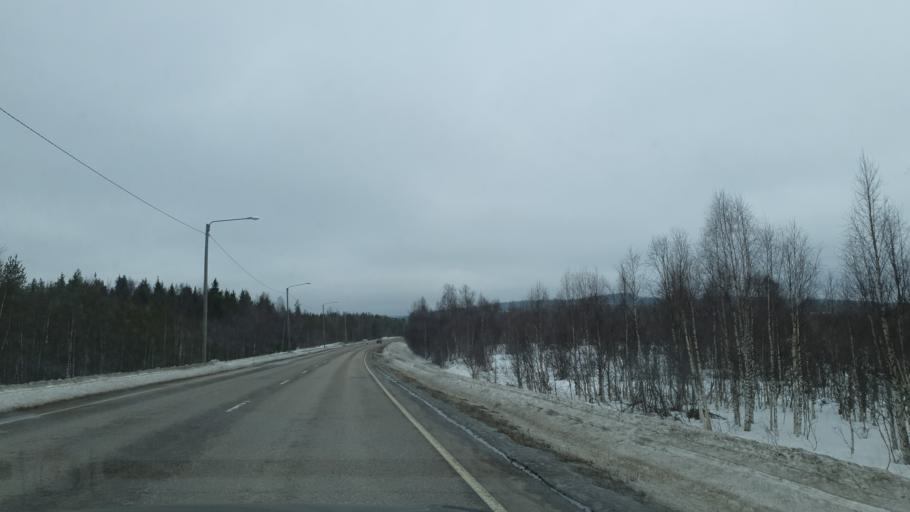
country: FI
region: Lapland
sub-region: Torniolaakso
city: Pello
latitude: 66.8990
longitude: 24.0924
